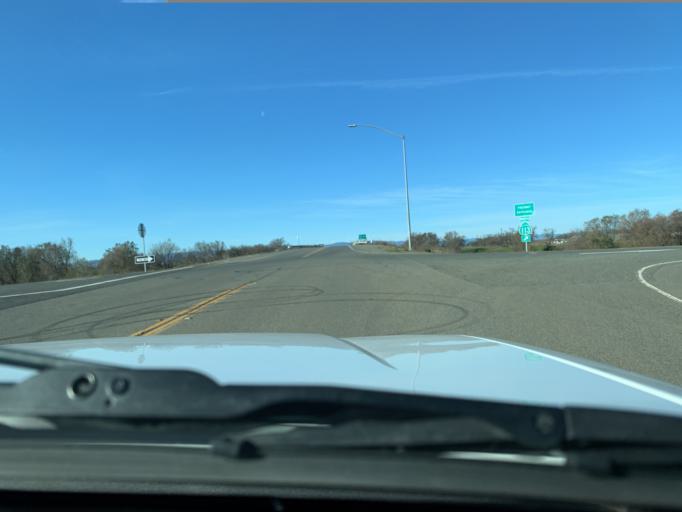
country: US
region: California
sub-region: Yolo County
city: Woodland
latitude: 38.6410
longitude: -121.7574
